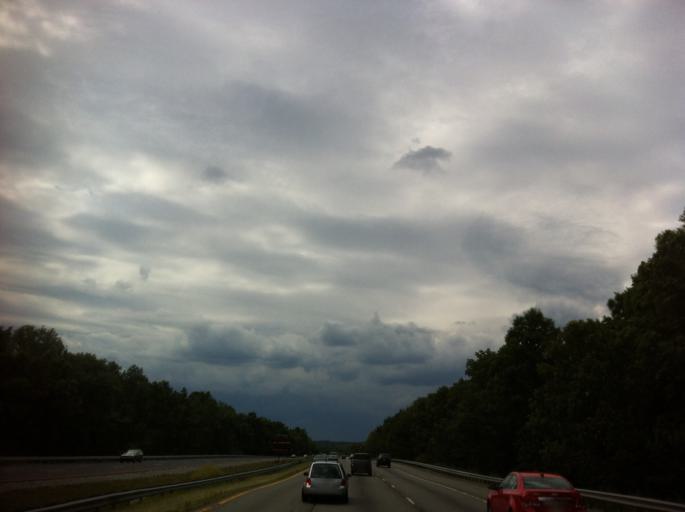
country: US
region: New Jersey
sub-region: Passaic County
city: Singac
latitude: 40.8995
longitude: -74.2407
